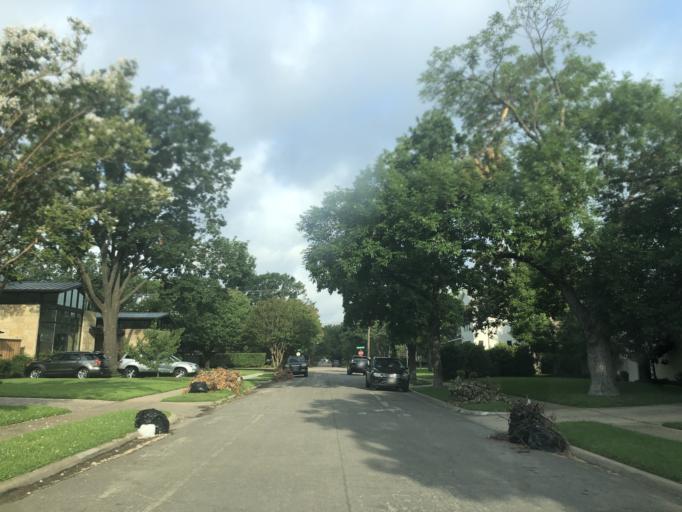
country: US
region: Texas
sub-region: Dallas County
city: University Park
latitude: 32.8562
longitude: -96.8143
